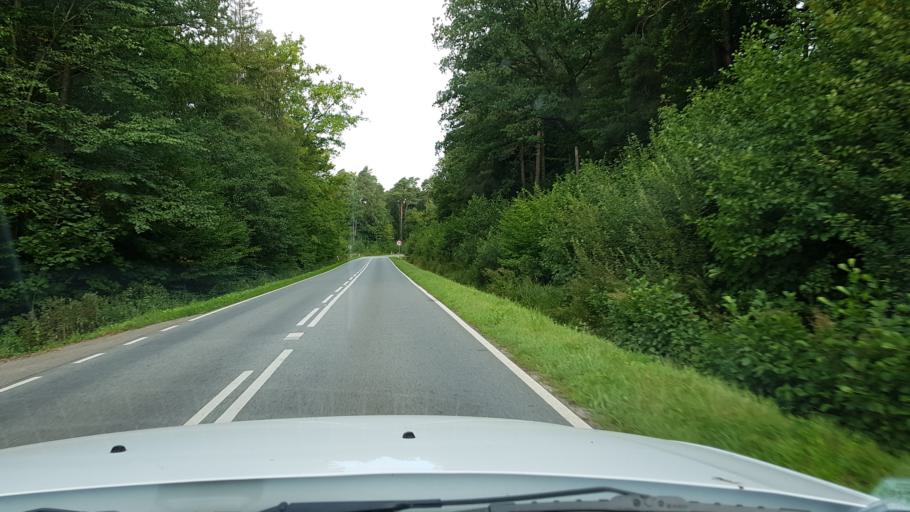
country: PL
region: West Pomeranian Voivodeship
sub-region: Powiat slawienski
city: Slawno
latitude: 54.3811
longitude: 16.6212
